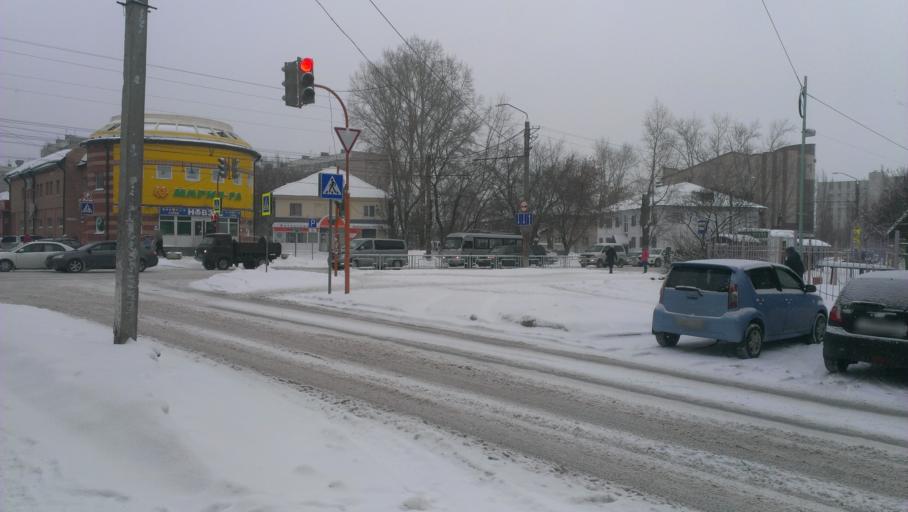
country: RU
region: Altai Krai
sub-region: Gorod Barnaulskiy
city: Barnaul
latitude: 53.3698
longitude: 83.6899
